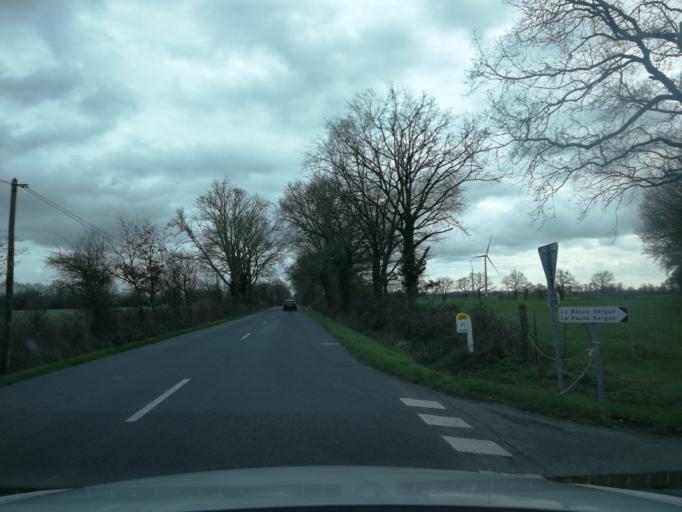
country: FR
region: Pays de la Loire
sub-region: Departement de la Loire-Atlantique
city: Montbert
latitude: 47.0179
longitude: -1.4861
